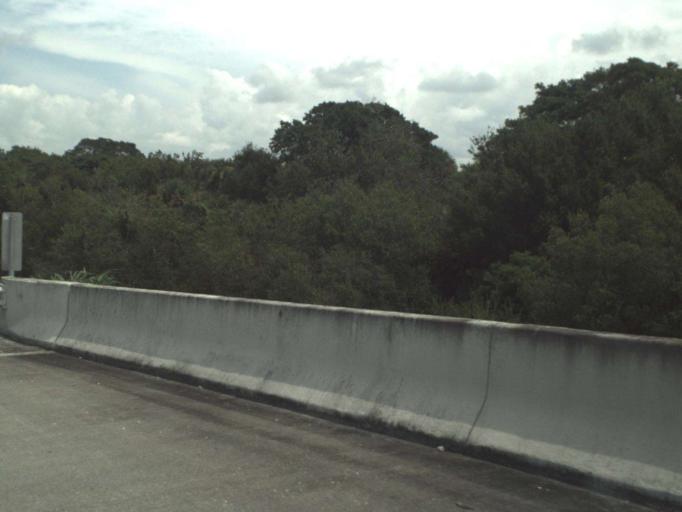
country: US
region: Florida
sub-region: Martin County
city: Indiantown
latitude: 26.9885
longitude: -80.6180
